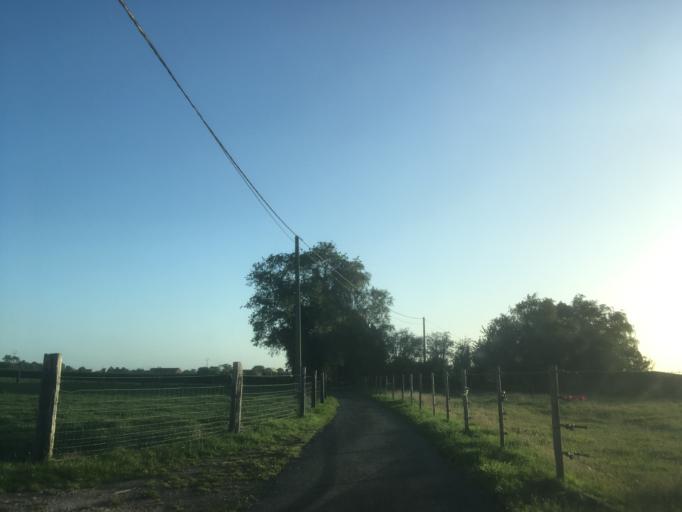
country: BE
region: Flanders
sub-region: Provincie West-Vlaanderen
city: Ichtegem
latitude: 51.0886
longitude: 3.0424
